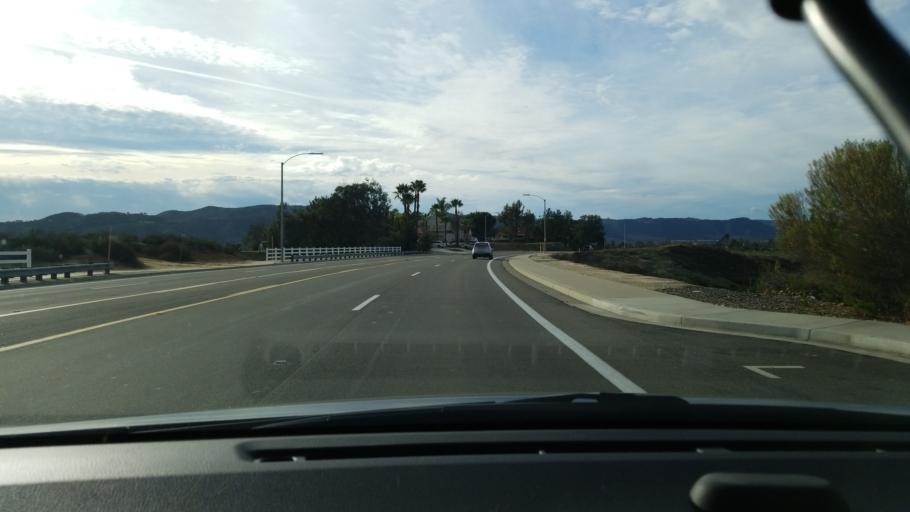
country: US
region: California
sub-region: Riverside County
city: Temecula
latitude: 33.4963
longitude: -117.1247
